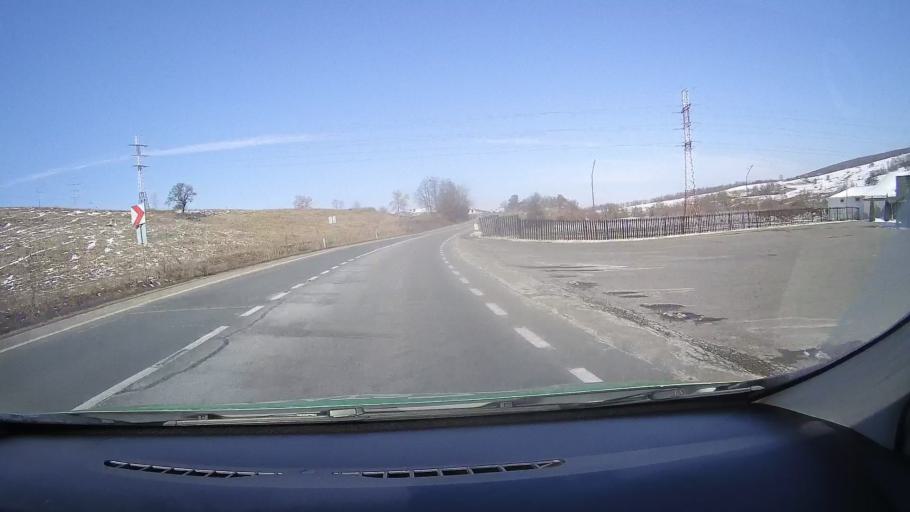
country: RO
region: Brasov
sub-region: Oras Rupea
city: Fiser
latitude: 46.0567
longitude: 25.1784
